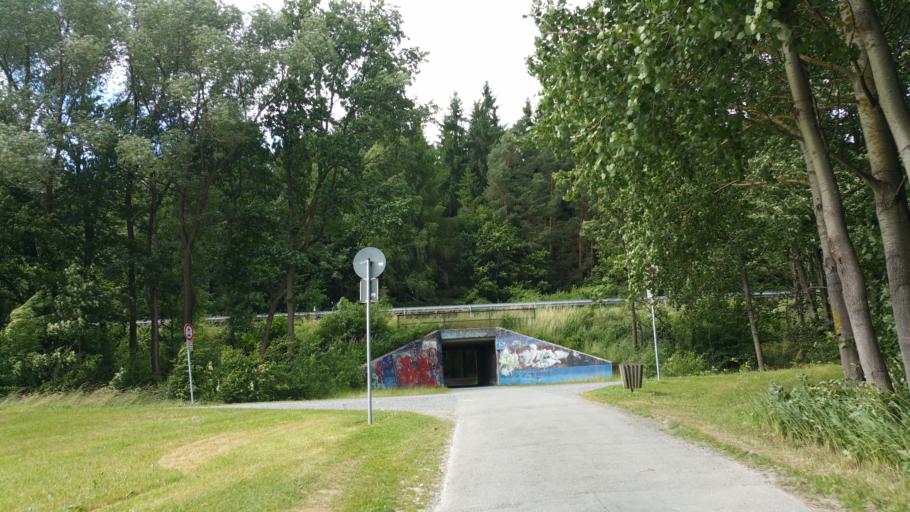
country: DE
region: Bavaria
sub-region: Upper Franconia
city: Hof
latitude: 50.2880
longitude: 11.9085
